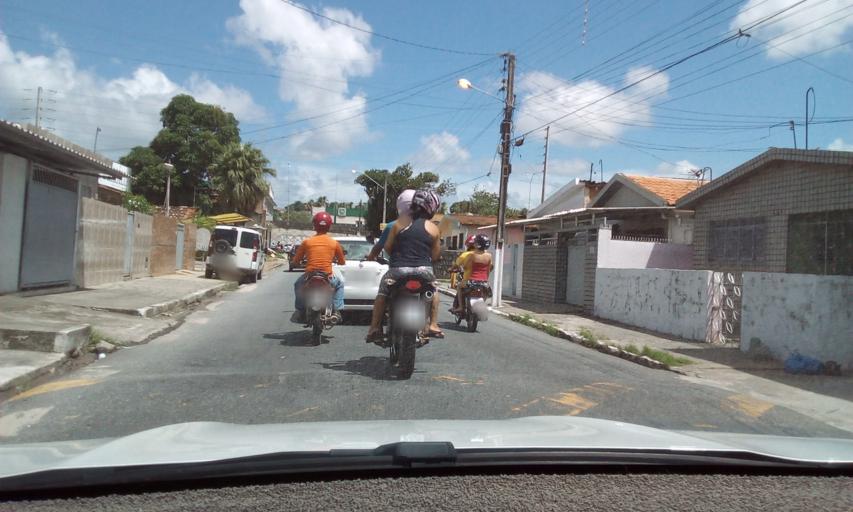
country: BR
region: Paraiba
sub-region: Bayeux
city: Bayeux
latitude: -7.1300
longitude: -34.9325
